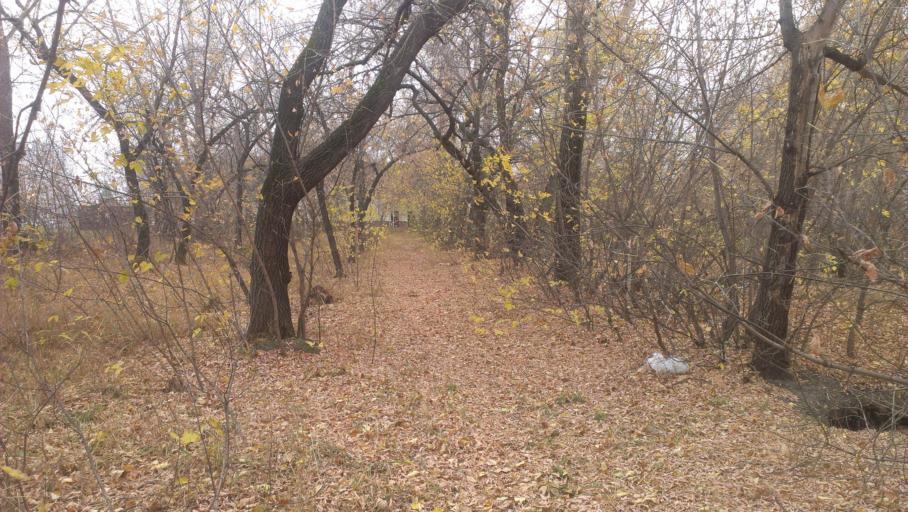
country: RU
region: Altai Krai
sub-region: Gorod Barnaulskiy
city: Barnaul
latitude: 53.3622
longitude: 83.6918
